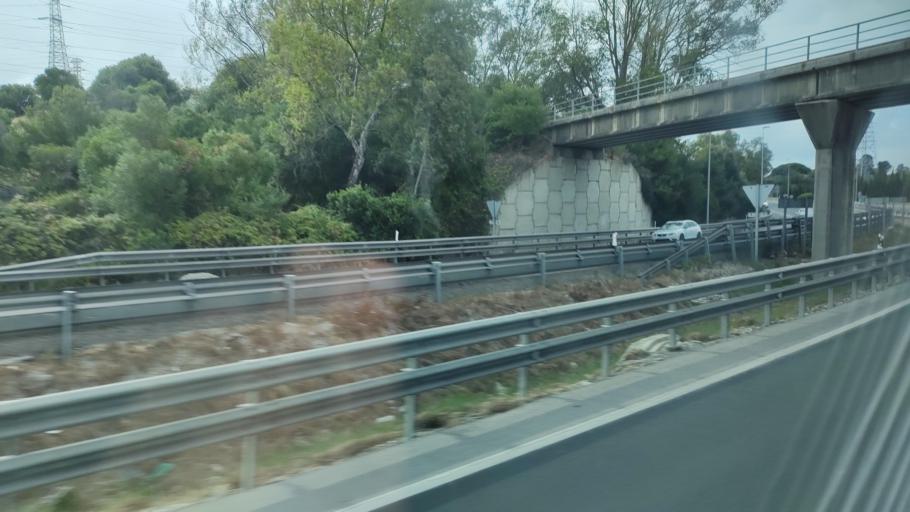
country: ES
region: Andalusia
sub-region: Provincia de Cadiz
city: San Roque
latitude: 36.1898
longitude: -5.3860
